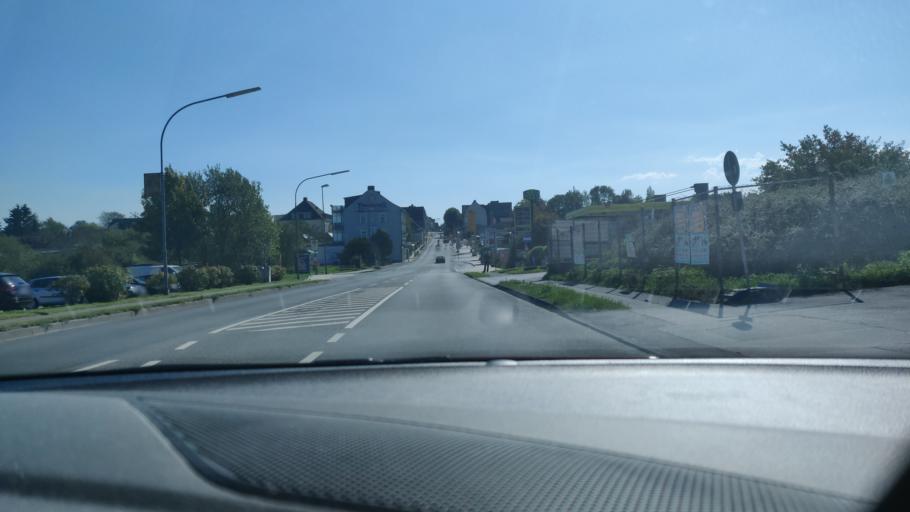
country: DE
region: North Rhine-Westphalia
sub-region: Regierungsbezirk Dusseldorf
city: Velbert
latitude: 51.3190
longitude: 7.0625
